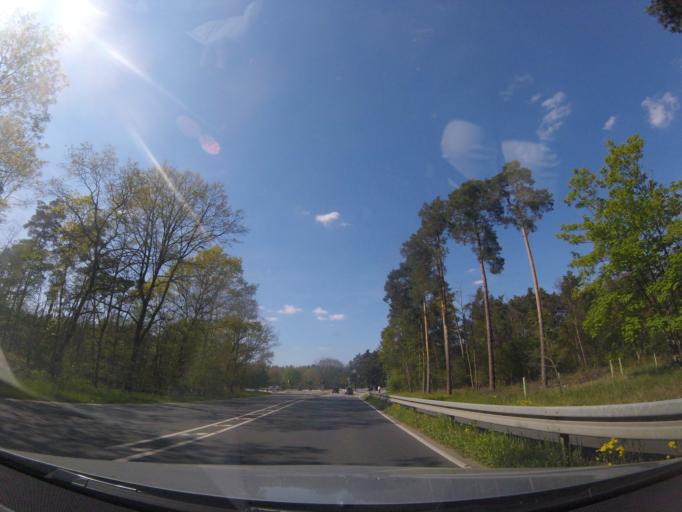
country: DE
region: Hesse
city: Pfungstadt
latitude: 49.8250
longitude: 8.5817
